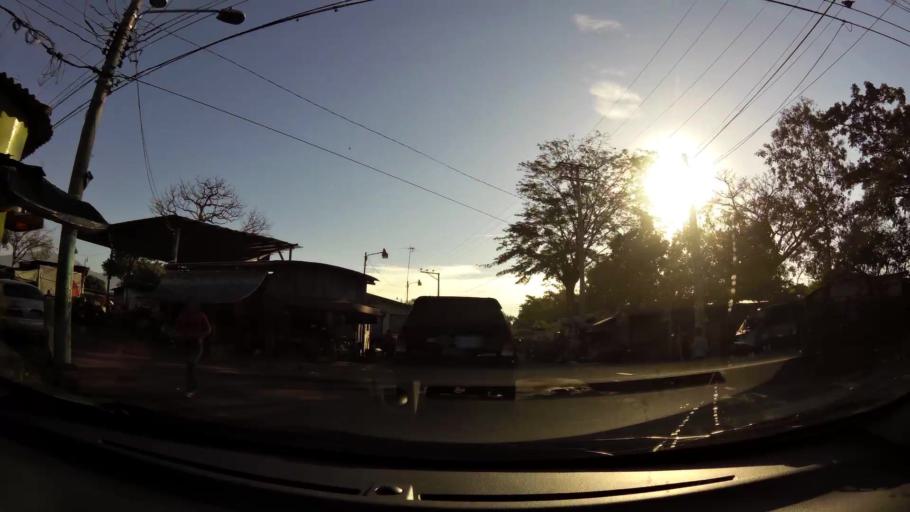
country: SV
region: Sonsonate
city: San Antonio del Monte
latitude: 13.7146
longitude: -89.7327
